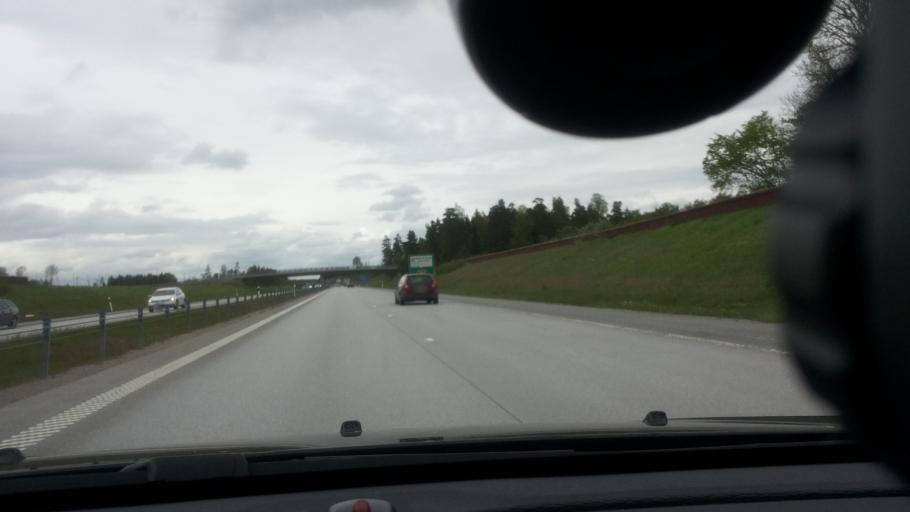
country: SE
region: Uppsala
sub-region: Uppsala Kommun
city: Gamla Uppsala
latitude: 59.9203
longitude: 17.6540
